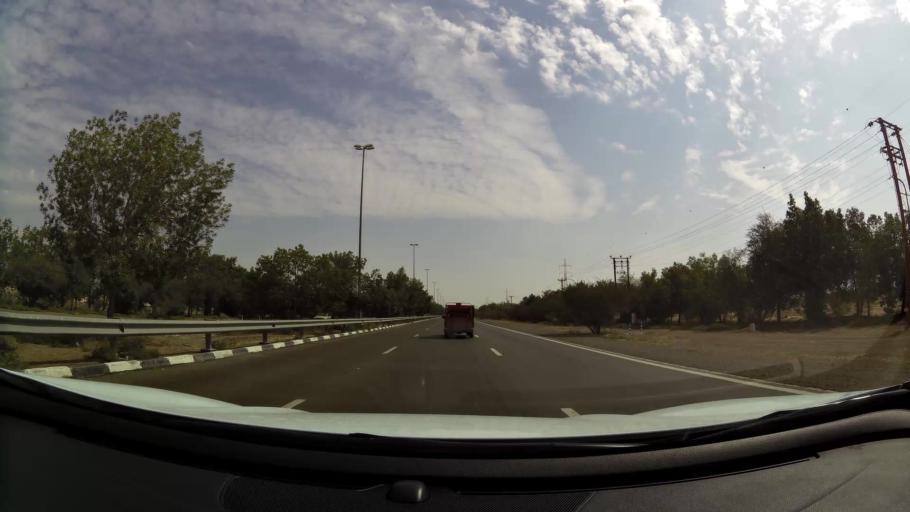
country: AE
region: Abu Dhabi
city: Al Ain
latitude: 24.1405
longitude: 55.8147
